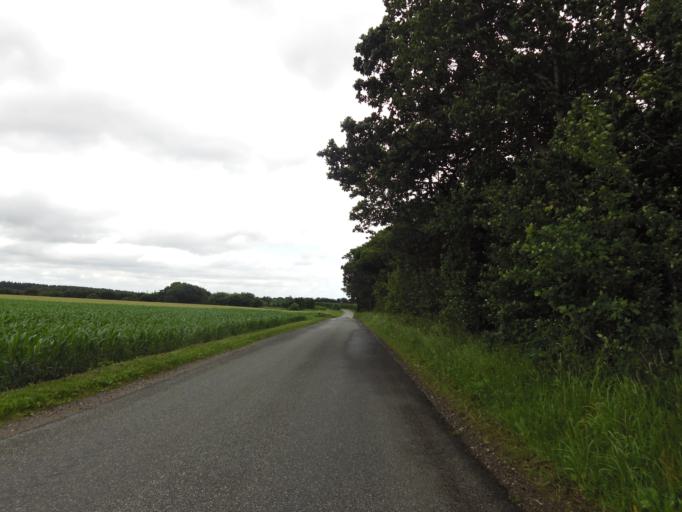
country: DK
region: South Denmark
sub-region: Kolding Kommune
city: Vamdrup
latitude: 55.3406
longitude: 9.1965
